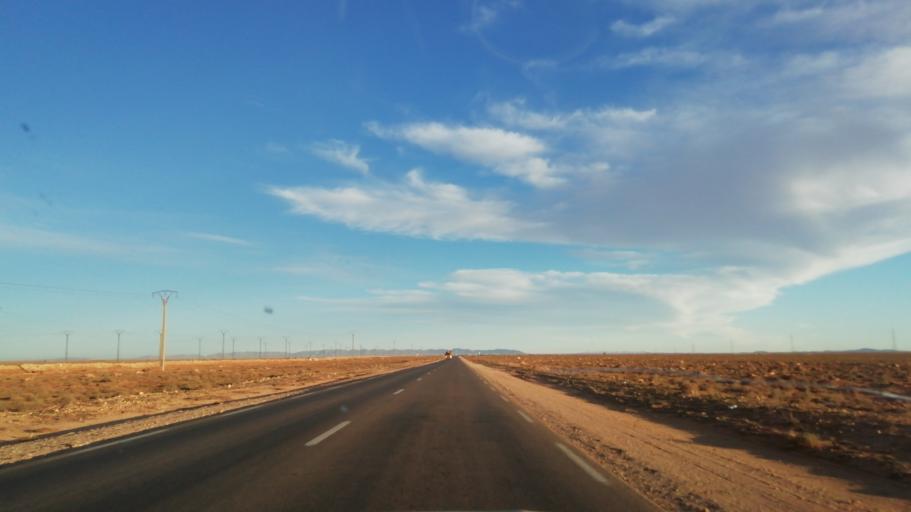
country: DZ
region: Wilaya de Naama
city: Naama
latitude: 33.7393
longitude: -0.7696
